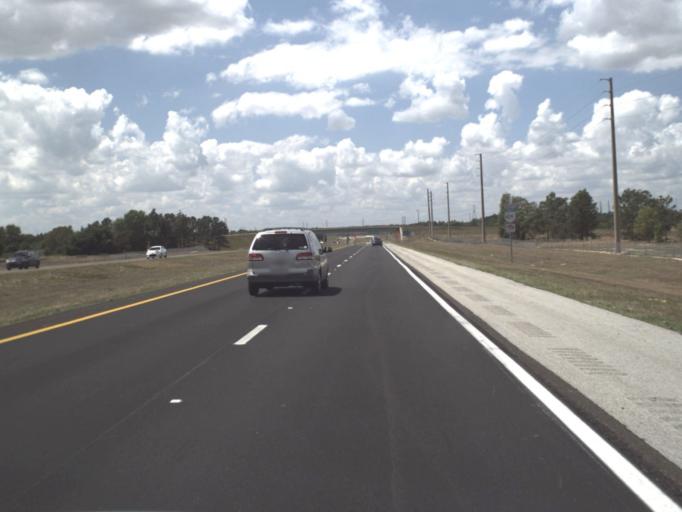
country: US
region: Florida
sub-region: Orange County
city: Oakland
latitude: 28.4931
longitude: -81.6221
